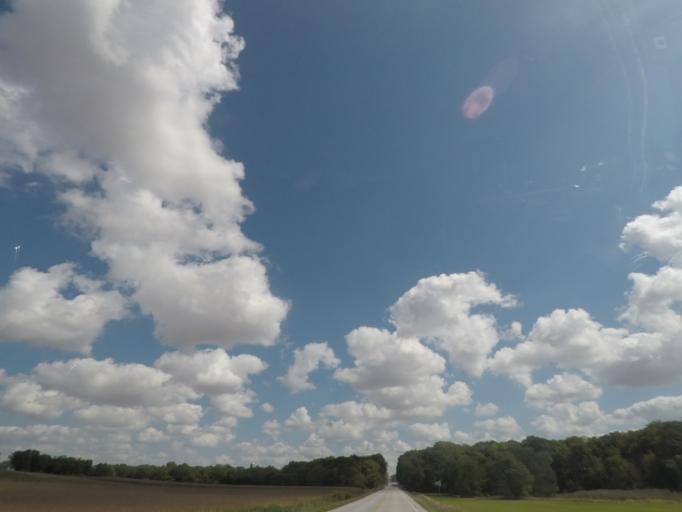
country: US
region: Iowa
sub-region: Story County
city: Nevada
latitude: 42.0777
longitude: -93.3598
